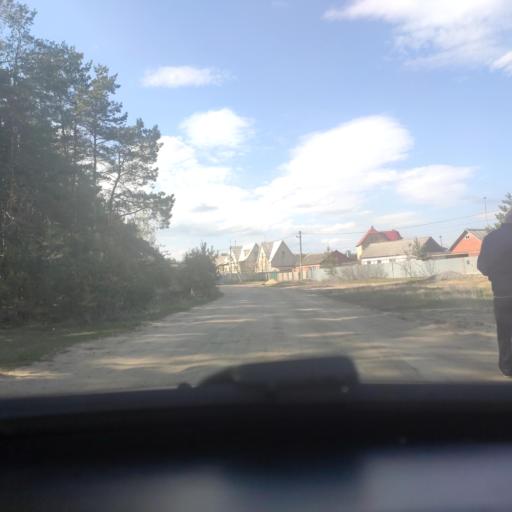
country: RU
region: Voronezj
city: Somovo
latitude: 51.7514
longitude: 39.3225
